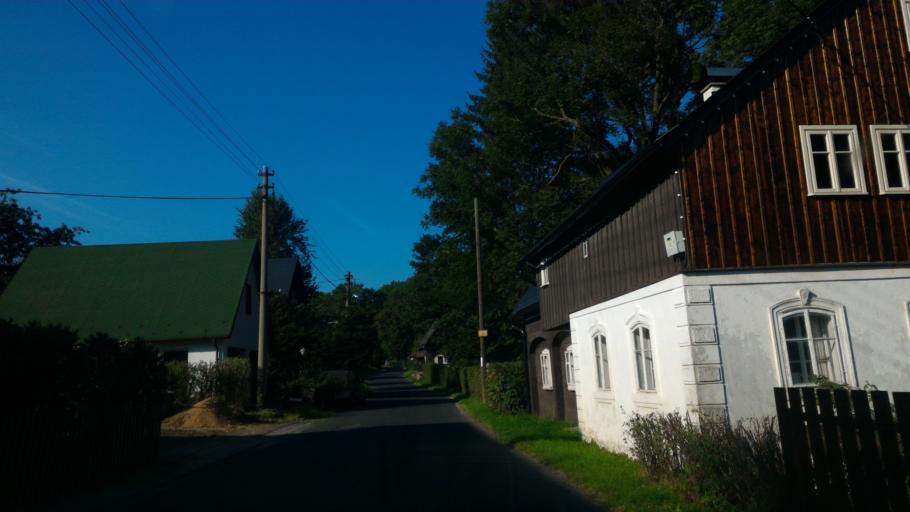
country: DE
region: Saxony
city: Kurort Jonsdorf
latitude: 50.8282
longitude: 14.6678
